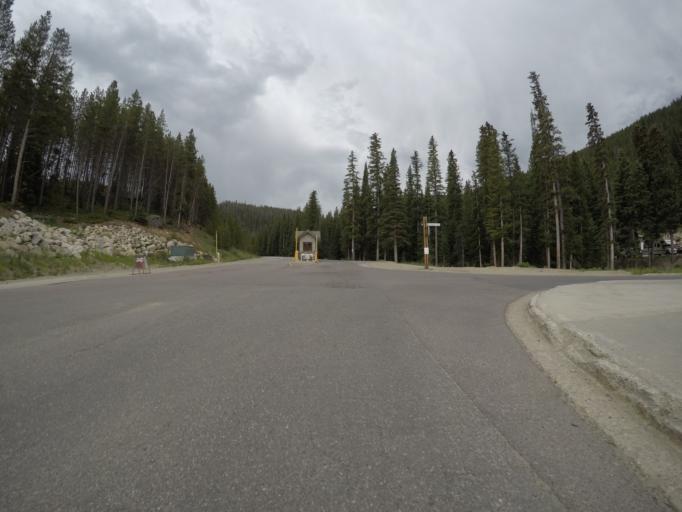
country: US
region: Colorado
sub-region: Grand County
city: Fraser
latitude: 39.8833
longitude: -105.7611
